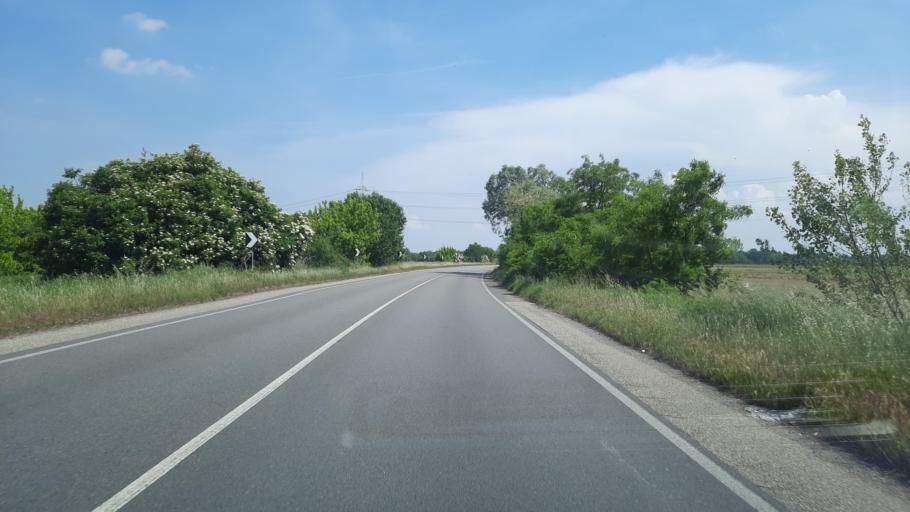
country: IT
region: Lombardy
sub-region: Provincia di Pavia
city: Dorno
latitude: 45.1859
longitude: 8.9589
